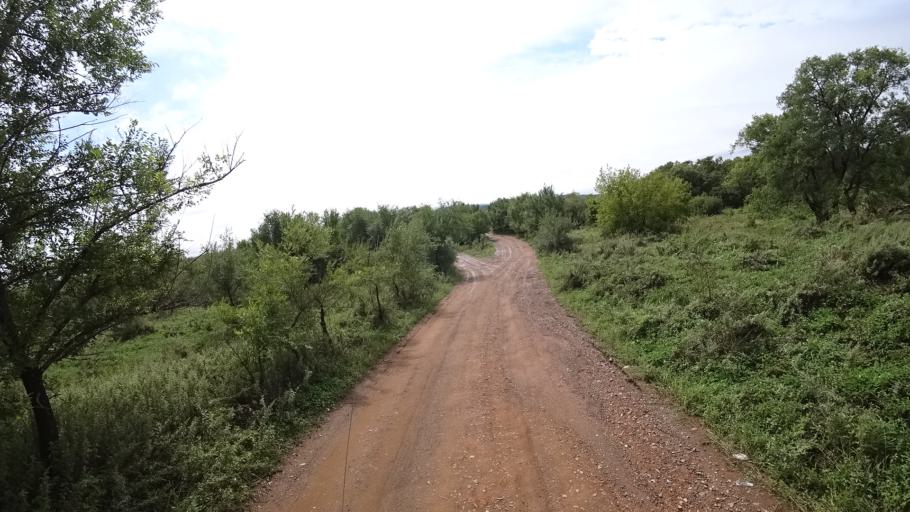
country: RU
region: Primorskiy
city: Monastyrishche
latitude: 44.1862
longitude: 132.4828
